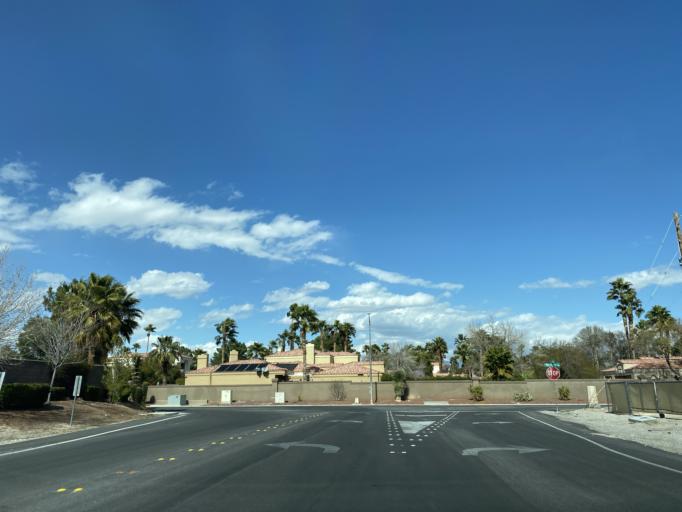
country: US
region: Nevada
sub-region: Clark County
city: Las Vegas
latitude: 36.2549
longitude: -115.2604
